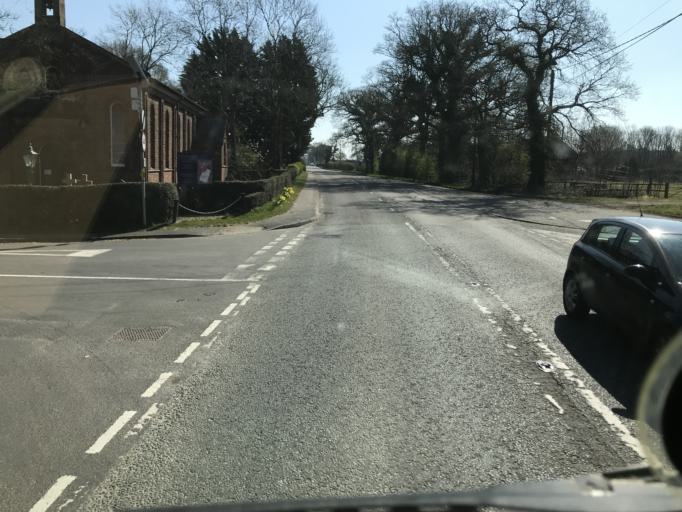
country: GB
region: England
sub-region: Cheshire East
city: Mobberley
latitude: 53.2781
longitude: -2.3026
